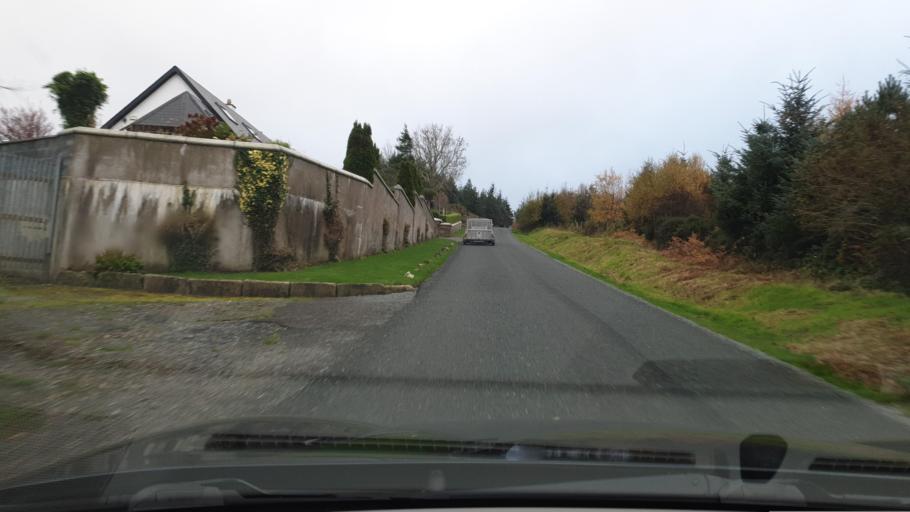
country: IE
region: Leinster
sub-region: Wicklow
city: Enniskerry
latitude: 53.1545
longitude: -6.1868
